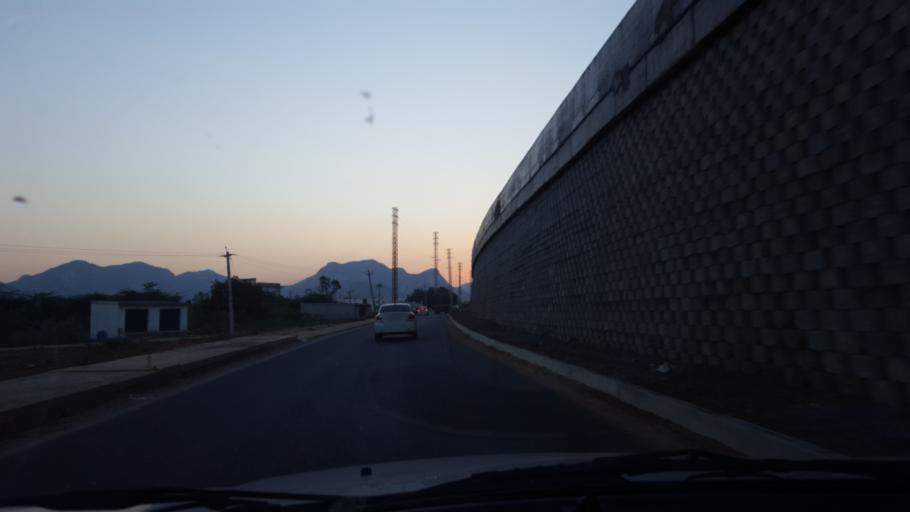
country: IN
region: Andhra Pradesh
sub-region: Chittoor
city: Narasingapuram
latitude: 13.5873
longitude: 79.3412
